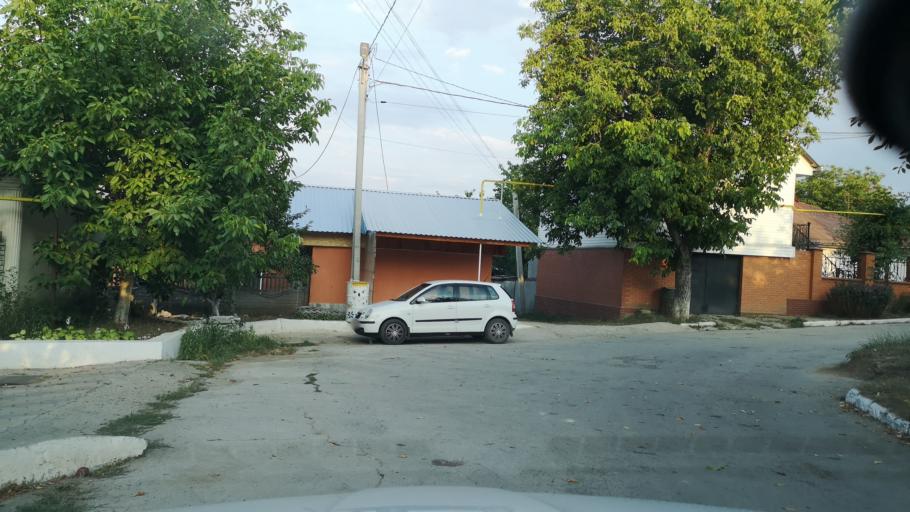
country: MD
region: Rezina
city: Rezina
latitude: 47.7544
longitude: 28.9586
